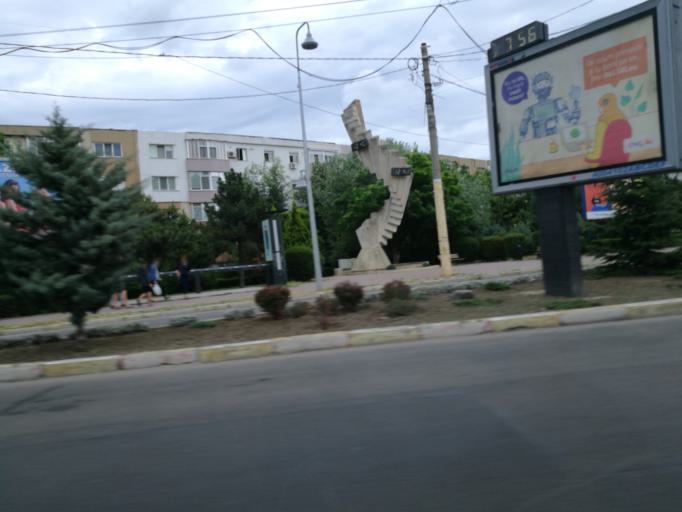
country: RO
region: Constanta
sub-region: Municipiul Constanta
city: Constanta
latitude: 44.1971
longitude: 28.6318
